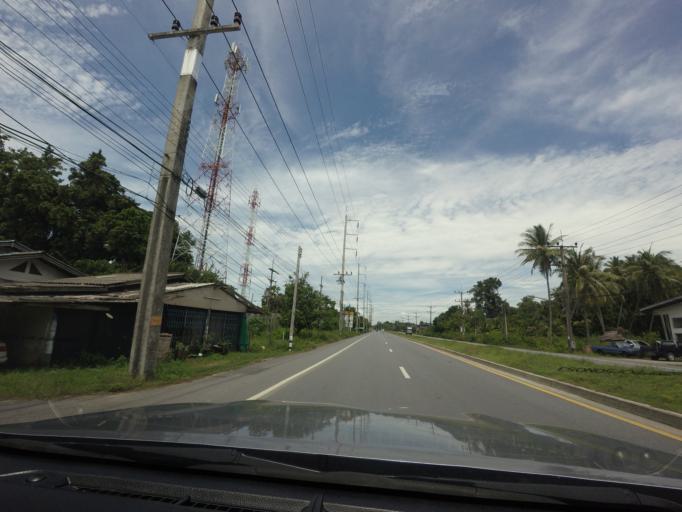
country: TH
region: Songkhla
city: Krasae Sin
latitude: 7.6085
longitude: 100.3993
